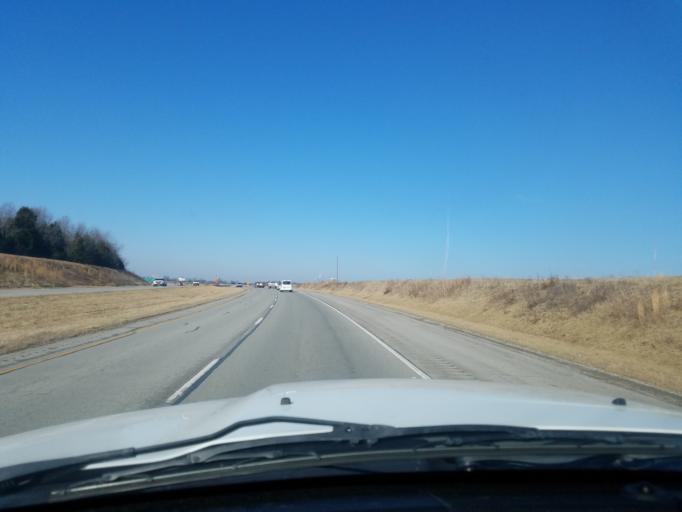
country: US
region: Kentucky
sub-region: Hardin County
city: Elizabethtown
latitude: 37.6667
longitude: -85.8406
